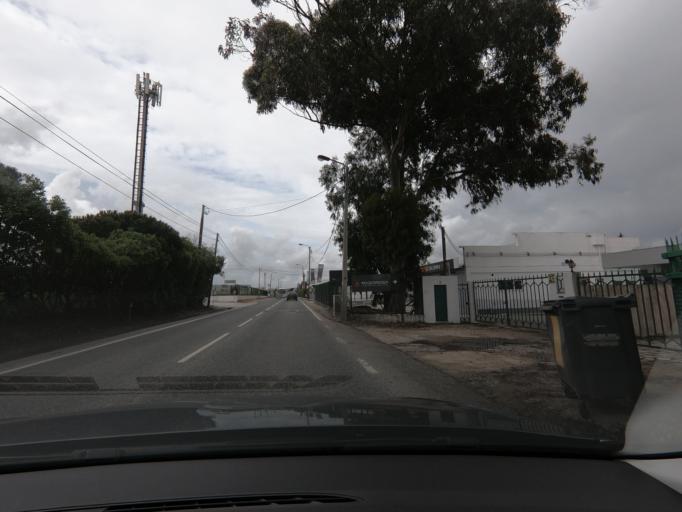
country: PT
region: Lisbon
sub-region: Sintra
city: Rio de Mouro
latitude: 38.7431
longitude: -9.3415
